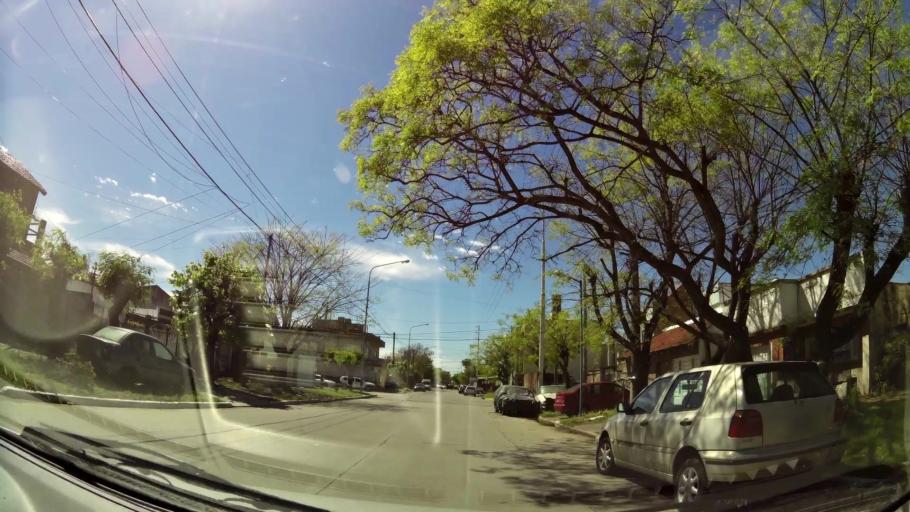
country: AR
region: Buenos Aires
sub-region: Partido de Quilmes
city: Quilmes
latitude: -34.7012
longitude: -58.2828
